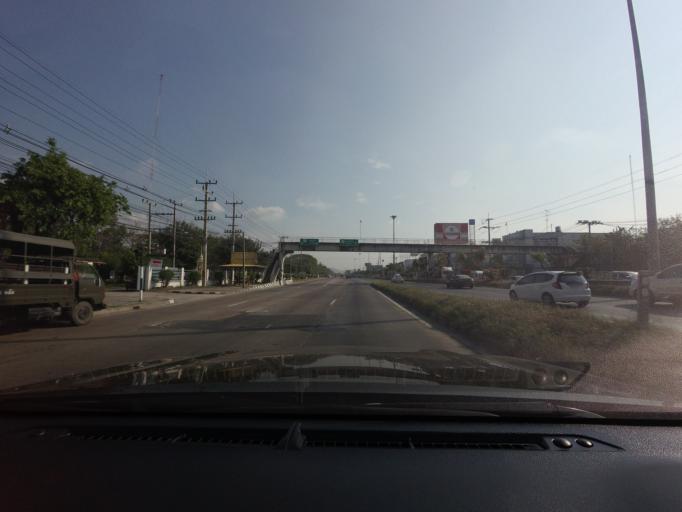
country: TH
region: Sara Buri
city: Saraburi
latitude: 14.5170
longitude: 100.9155
